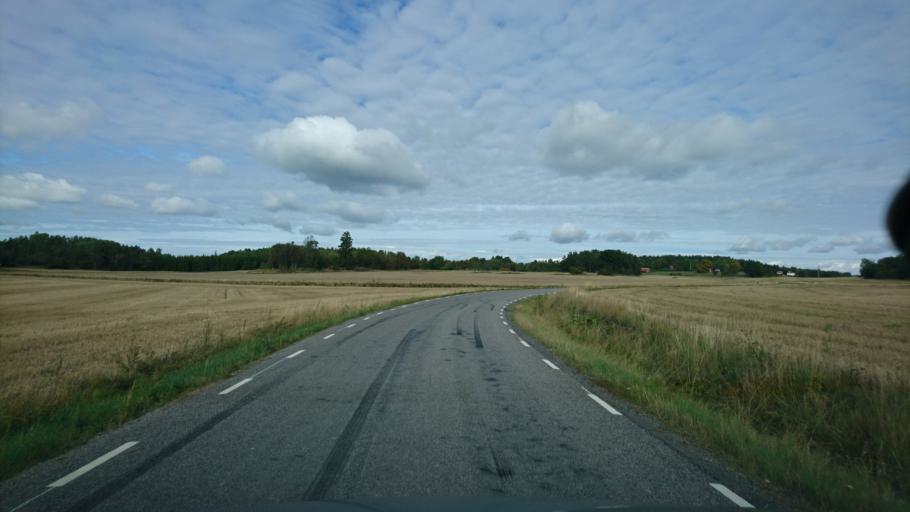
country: SE
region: Soedermanland
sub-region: Strangnas Kommun
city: Stallarholmen
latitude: 59.3808
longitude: 17.2599
